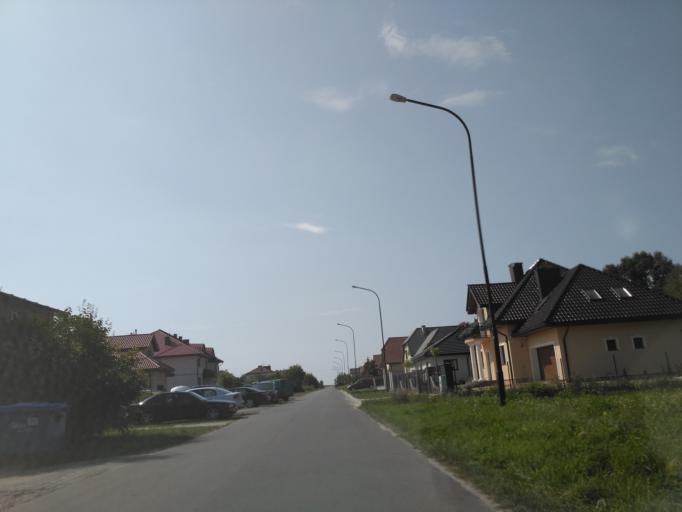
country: PL
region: Lublin Voivodeship
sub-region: Powiat lubelski
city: Lublin
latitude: 51.1740
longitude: 22.5838
